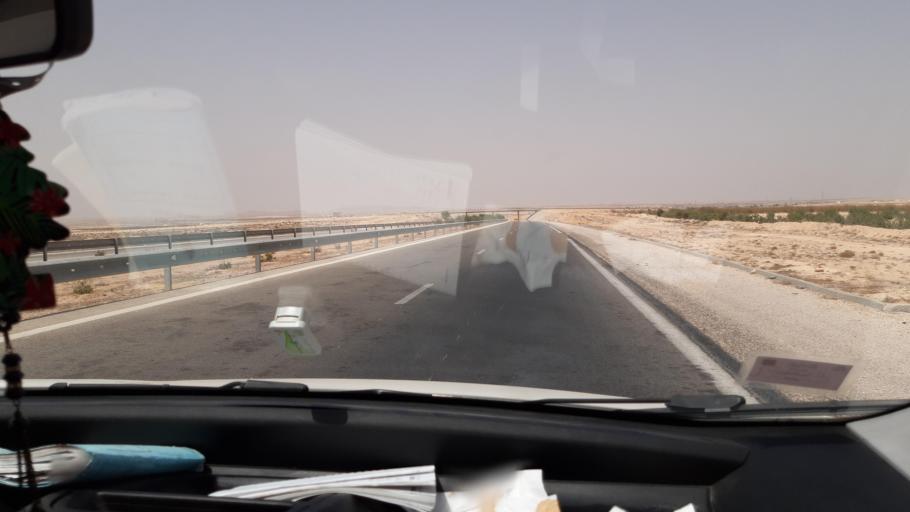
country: TN
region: Qabis
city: Gabes
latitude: 33.9558
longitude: 9.9574
